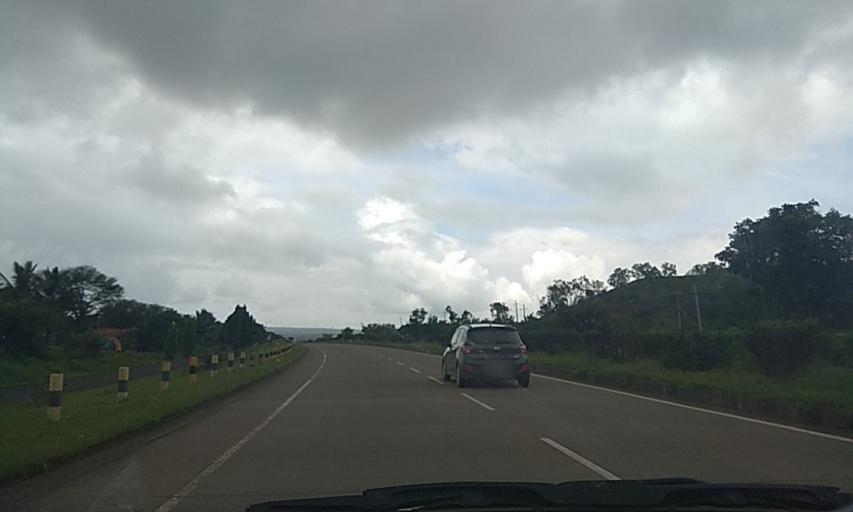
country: IN
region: Karnataka
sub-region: Belgaum
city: Sankeshwar
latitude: 16.2865
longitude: 74.4444
